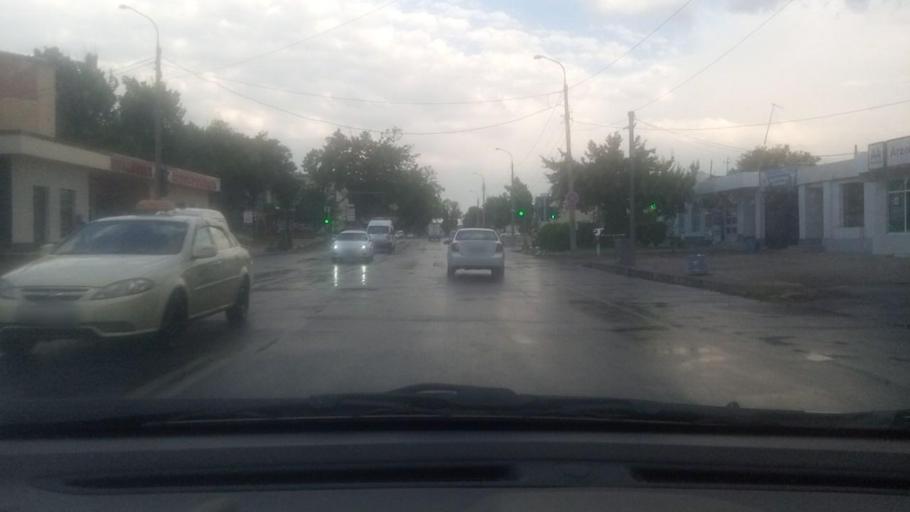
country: UZ
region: Toshkent Shahri
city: Tashkent
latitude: 41.2982
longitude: 69.1907
